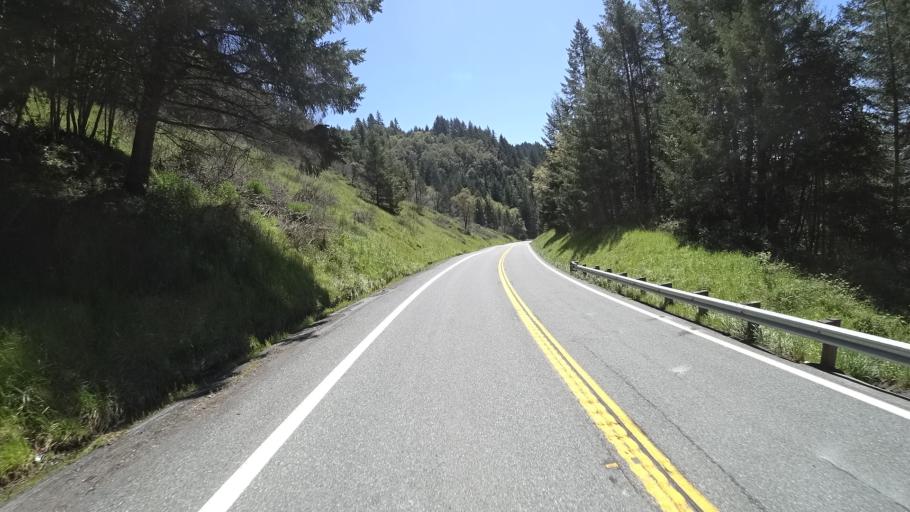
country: US
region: California
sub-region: Humboldt County
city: Willow Creek
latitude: 40.9219
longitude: -123.7950
